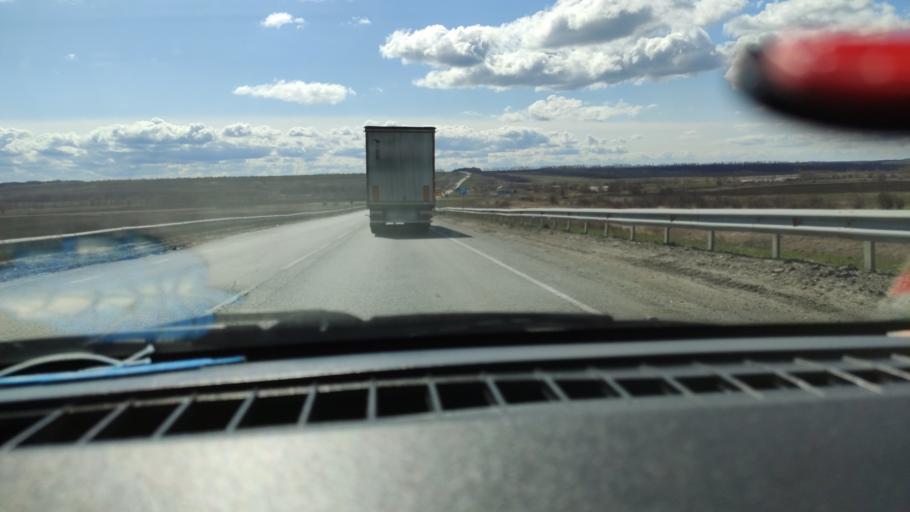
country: RU
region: Saratov
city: Dukhovnitskoye
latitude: 52.7438
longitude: 48.2527
